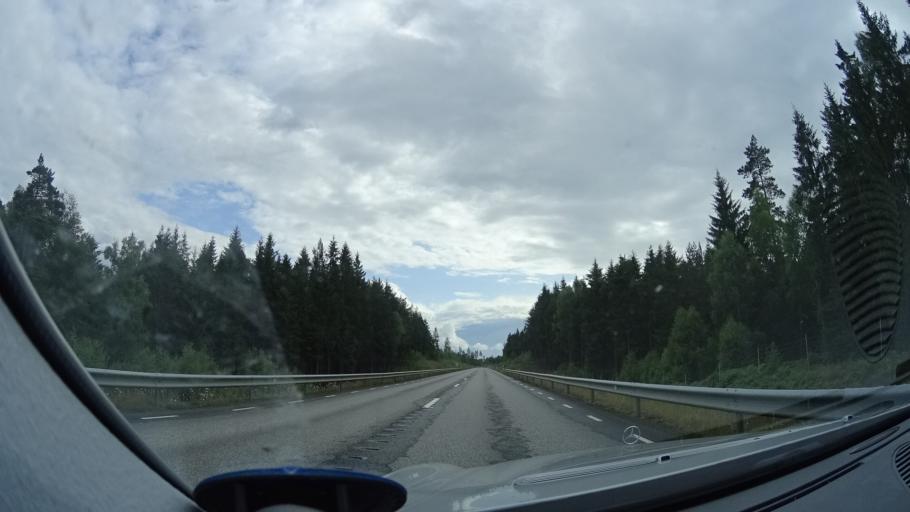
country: SE
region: Blekinge
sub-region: Karlshamns Kommun
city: Svangsta
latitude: 56.2801
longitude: 14.8660
